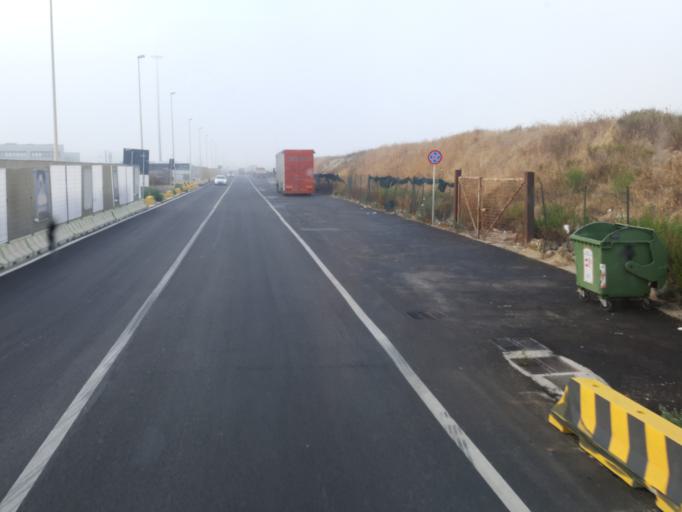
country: IT
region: Latium
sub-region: Citta metropolitana di Roma Capitale
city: Aurelia
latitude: 42.1141
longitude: 11.7700
